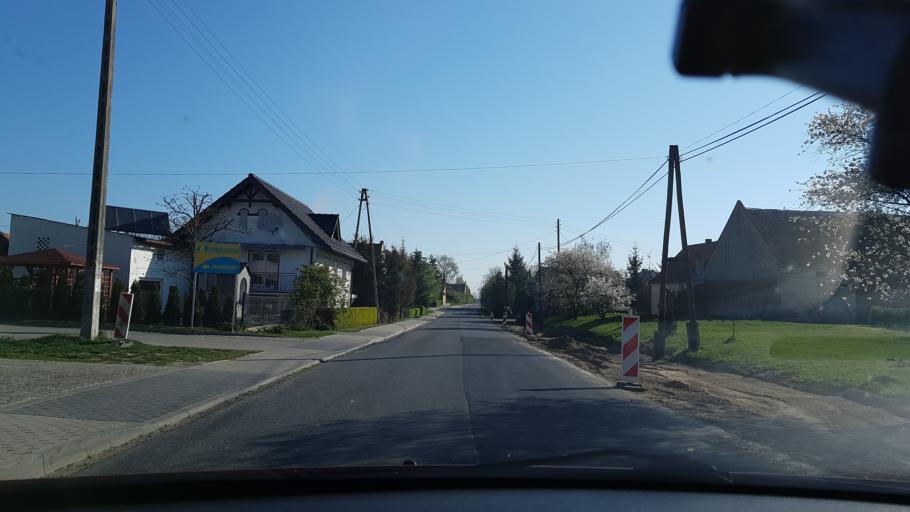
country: CZ
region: Olomoucky
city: Vidnava
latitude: 50.4195
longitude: 17.2245
